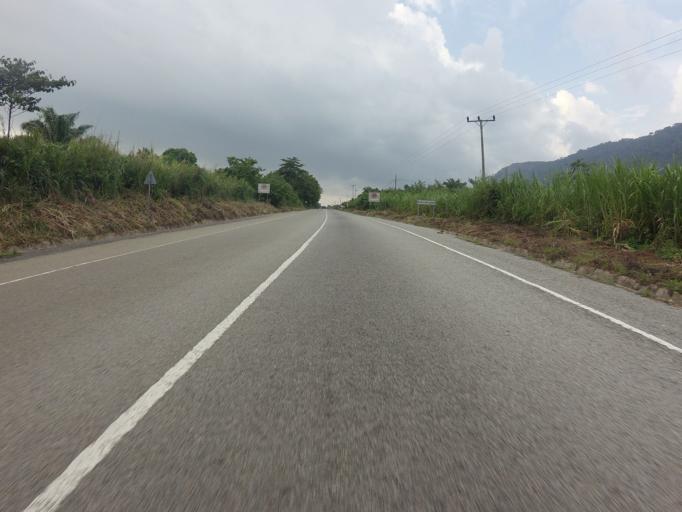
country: GH
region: Volta
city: Ho
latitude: 6.7630
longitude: 0.4800
